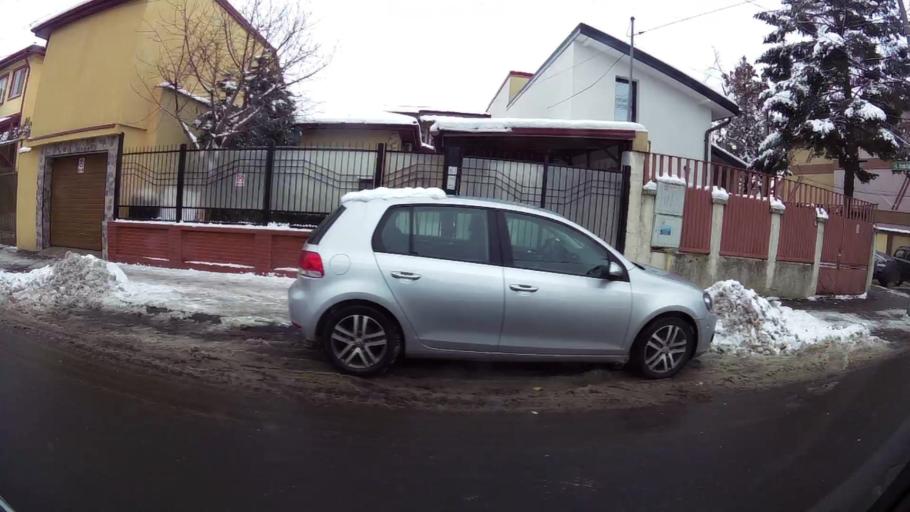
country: RO
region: Bucuresti
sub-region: Municipiul Bucuresti
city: Bucuresti
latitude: 44.3960
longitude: 26.1007
